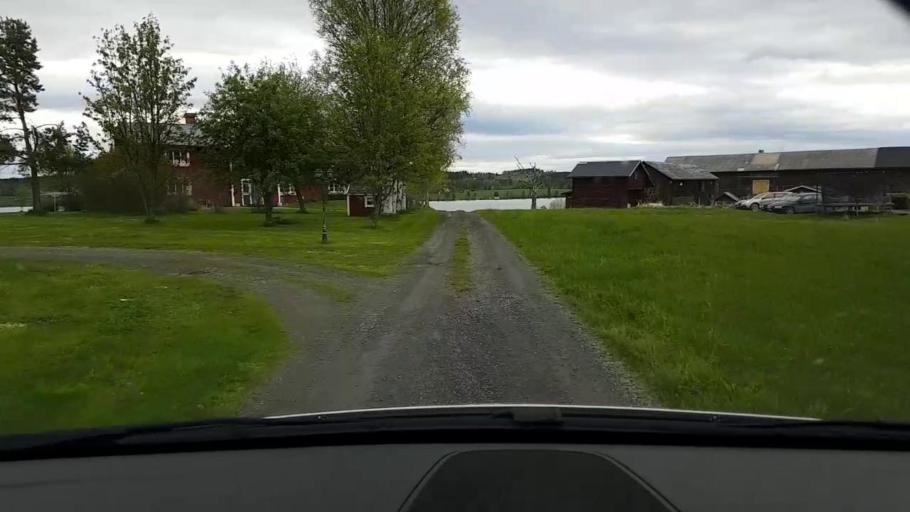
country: SE
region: Jaemtland
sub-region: Krokoms Kommun
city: Valla
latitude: 63.3026
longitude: 14.0432
